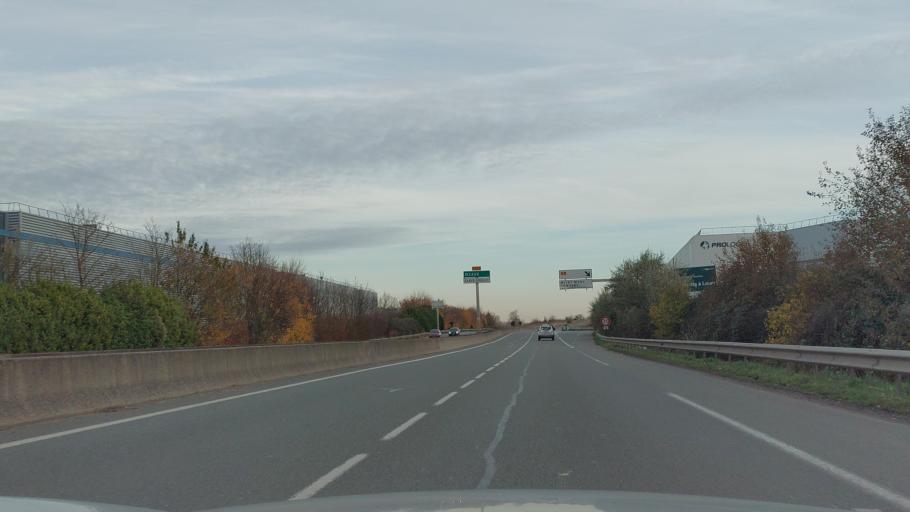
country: FR
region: Ile-de-France
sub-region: Departement de Seine-et-Marne
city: Mitry-Mory
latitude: 48.9950
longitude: 2.6499
